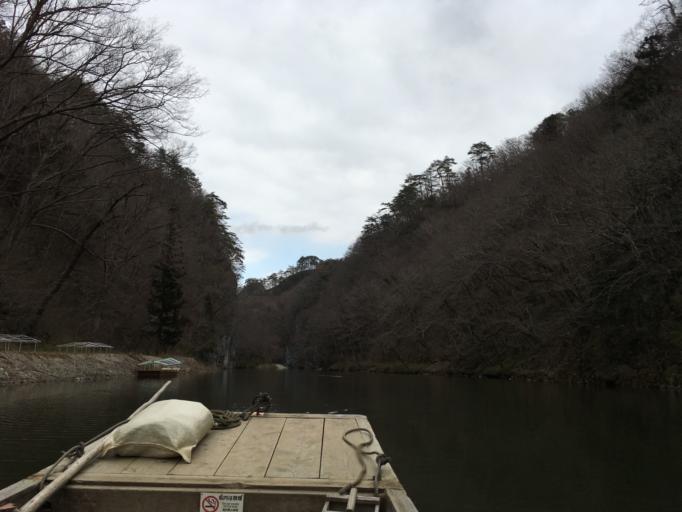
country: JP
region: Iwate
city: Ichinoseki
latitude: 38.9881
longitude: 141.2565
